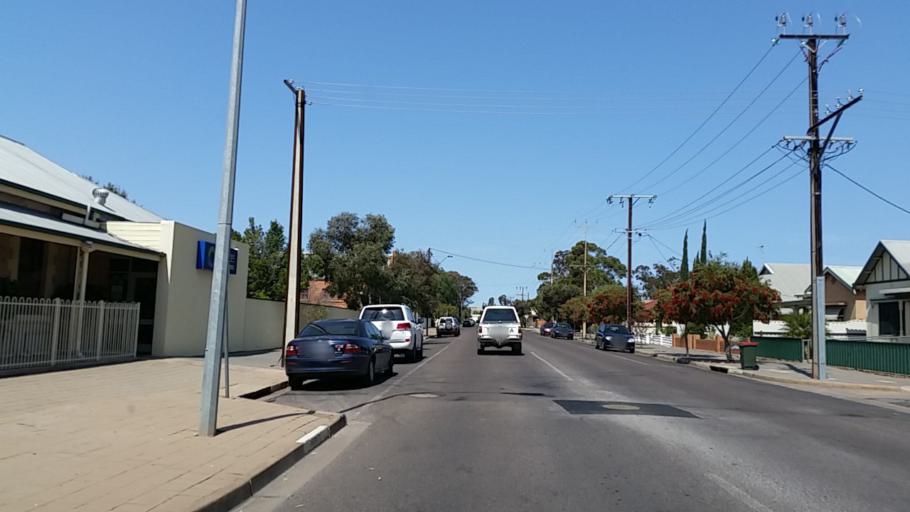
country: AU
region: South Australia
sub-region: Port Augusta
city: Port Augusta West
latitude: -32.4924
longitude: 137.7607
